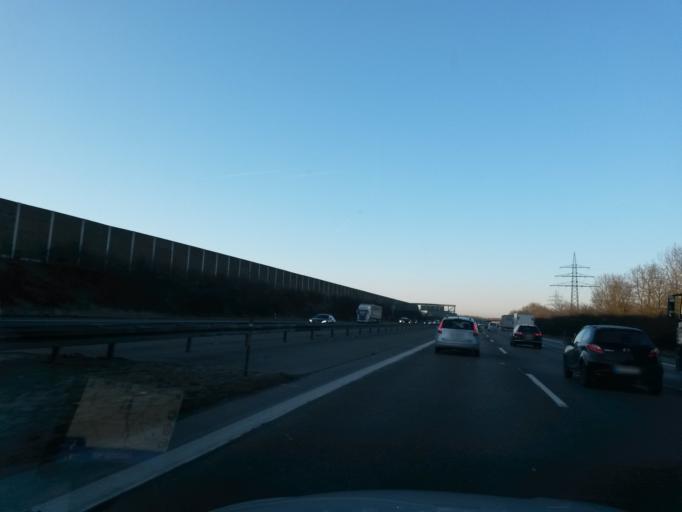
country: DE
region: Bavaria
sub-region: Upper Bavaria
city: Grasbrunn
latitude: 48.0841
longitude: 11.7394
